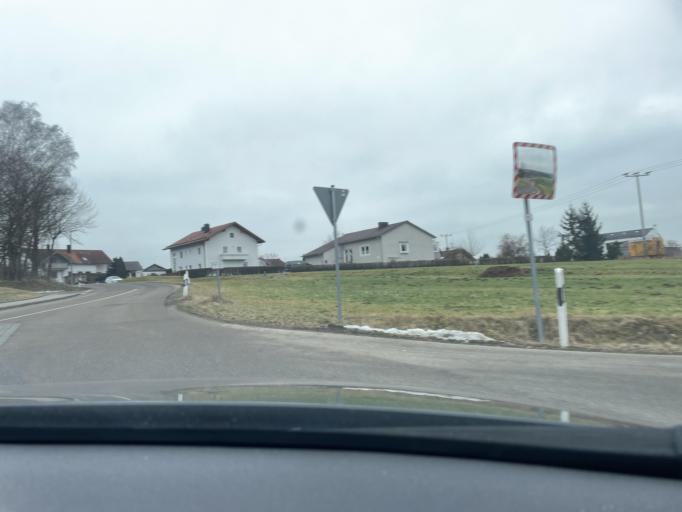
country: DE
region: Bavaria
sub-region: Upper Palatinate
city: Cham
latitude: 49.1938
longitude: 12.6858
